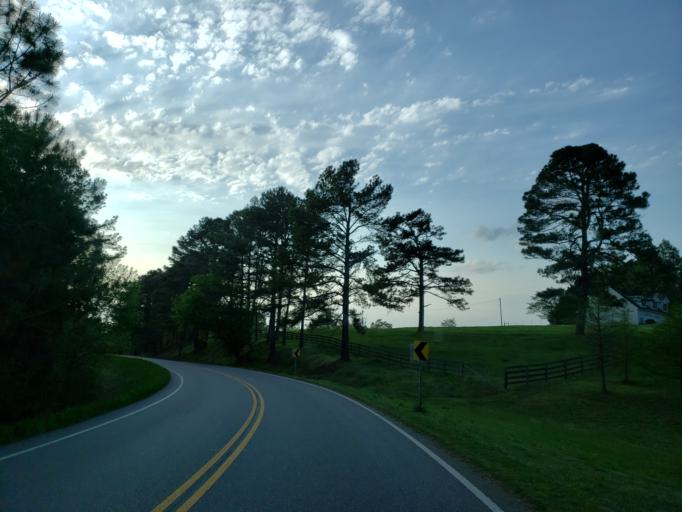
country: US
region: Georgia
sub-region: Cherokee County
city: Ball Ground
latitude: 34.2820
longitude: -84.3757
